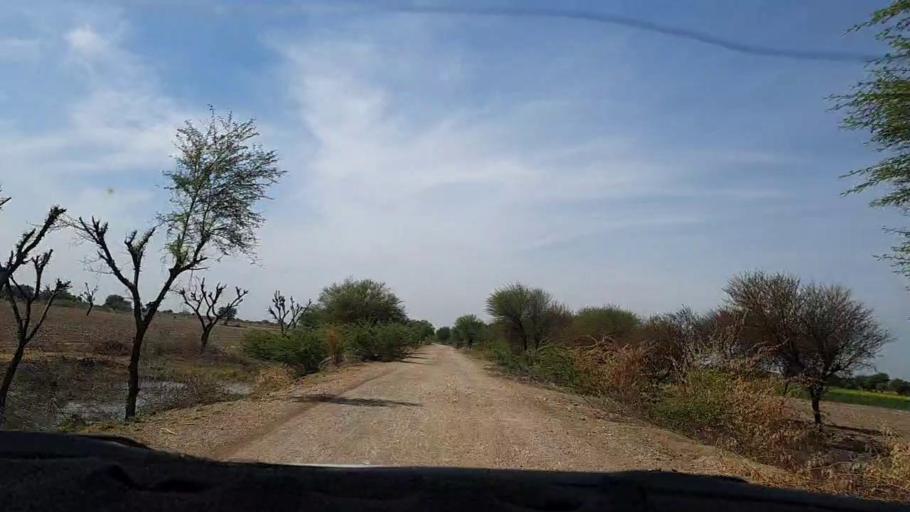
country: PK
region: Sindh
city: Pithoro
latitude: 25.5018
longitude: 69.4631
